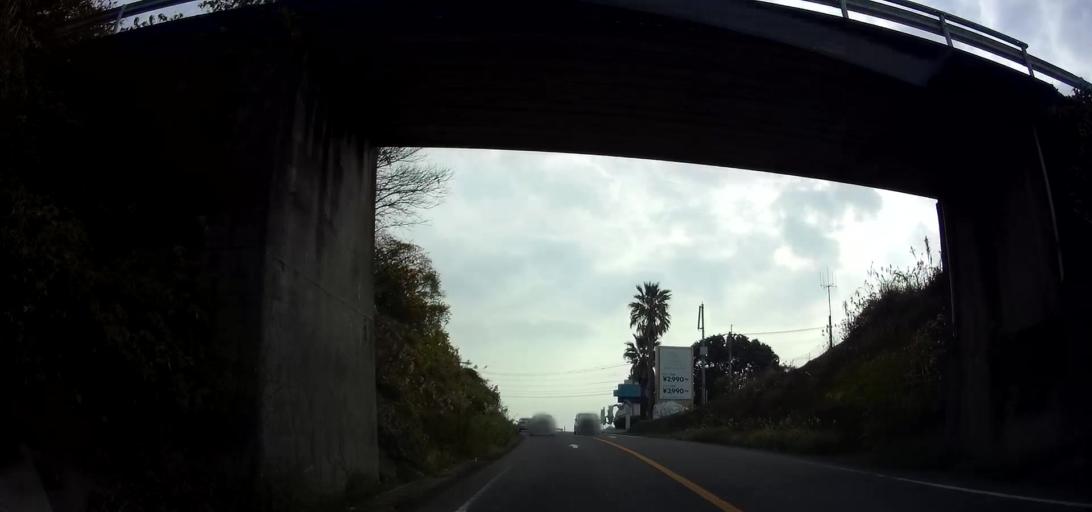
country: JP
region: Nagasaki
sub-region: Isahaya-shi
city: Isahaya
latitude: 32.7953
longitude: 130.0967
